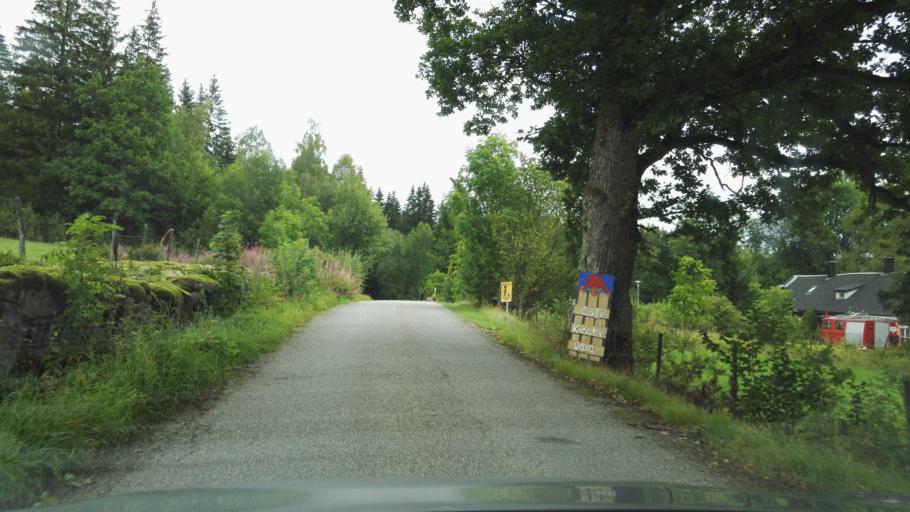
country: SE
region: Joenkoeping
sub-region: Vetlanda Kommun
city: Landsbro
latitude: 57.2332
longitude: 14.8317
